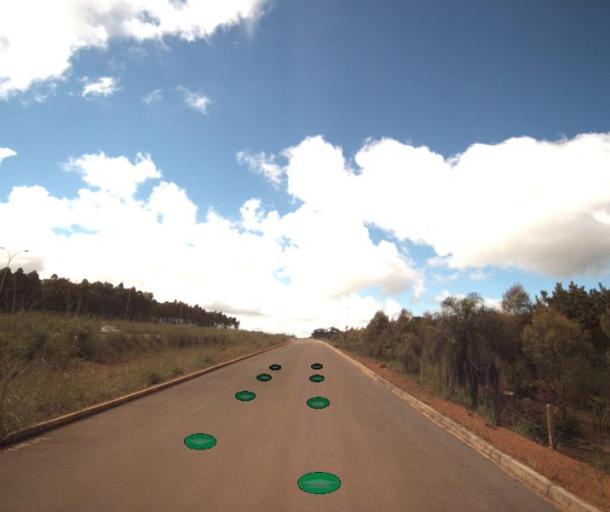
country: BR
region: Goias
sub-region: Anapolis
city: Anapolis
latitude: -16.2340
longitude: -49.0076
